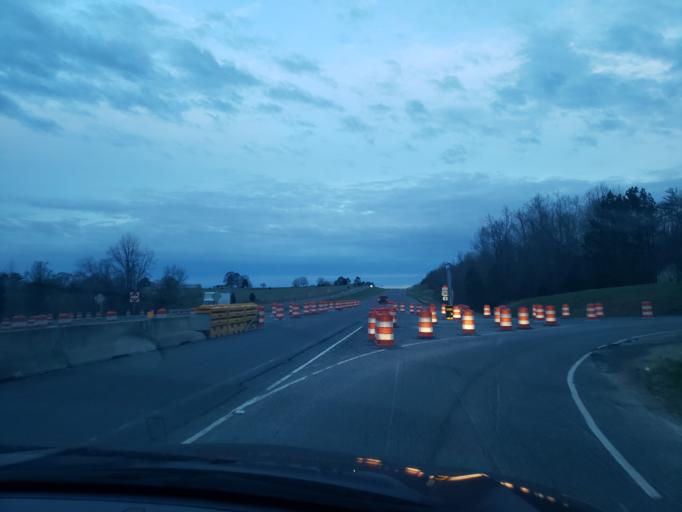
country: US
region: Alabama
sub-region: Lee County
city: Auburn
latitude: 32.6805
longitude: -85.4905
